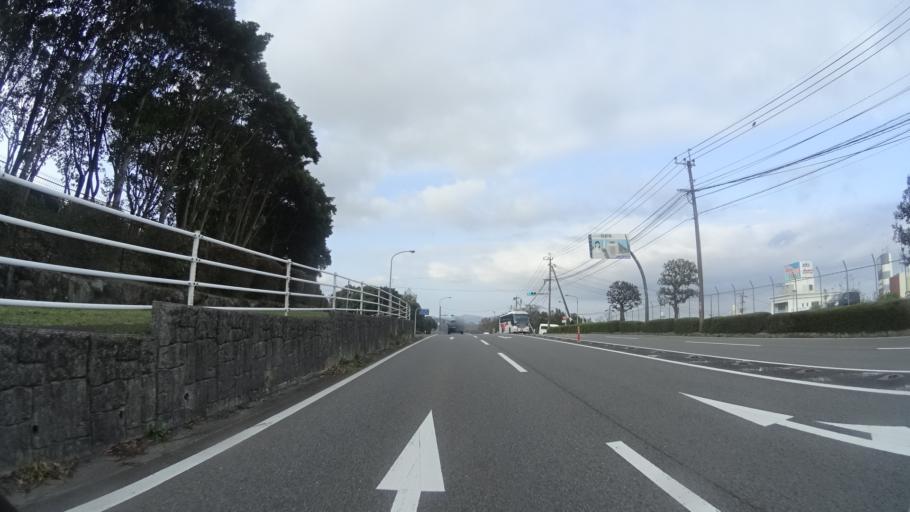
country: JP
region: Oita
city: Beppu
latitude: 33.2951
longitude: 131.4606
